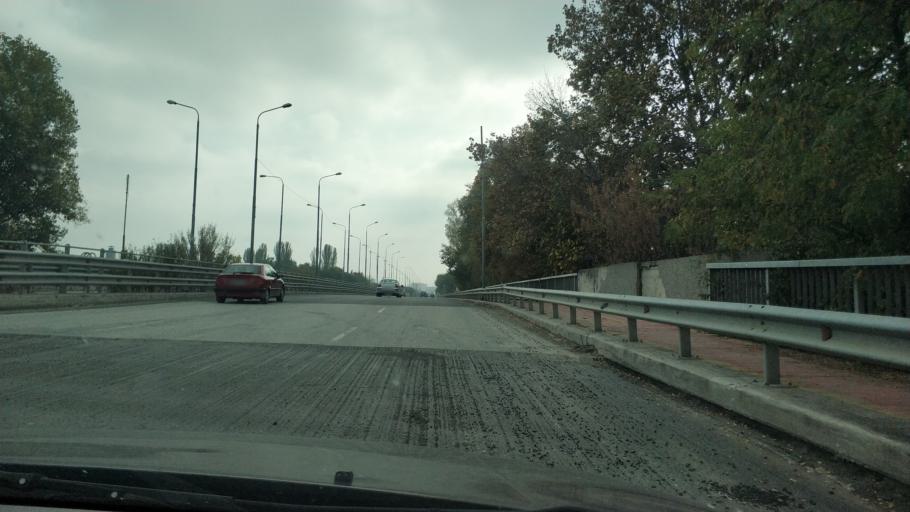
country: BG
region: Plovdiv
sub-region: Obshtina Plovdiv
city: Plovdiv
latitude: 42.1592
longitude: 24.7648
